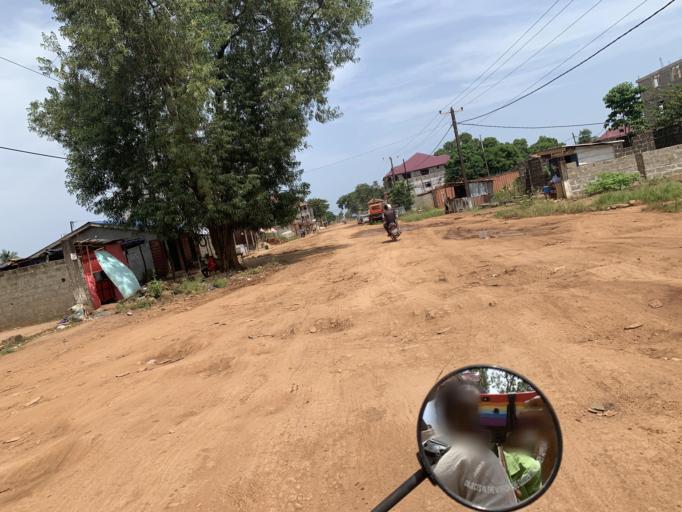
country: SL
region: Western Area
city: Hastings
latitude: 8.3998
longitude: -13.1393
